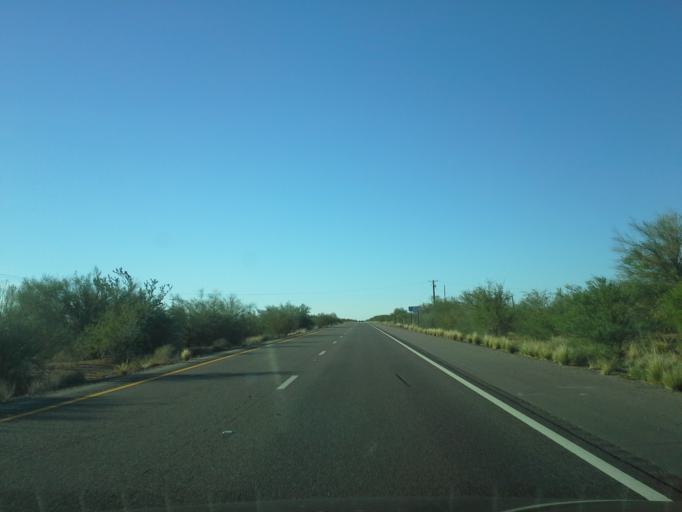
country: US
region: Arizona
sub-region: Pinal County
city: Gold Camp
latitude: 33.2993
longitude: -111.3950
